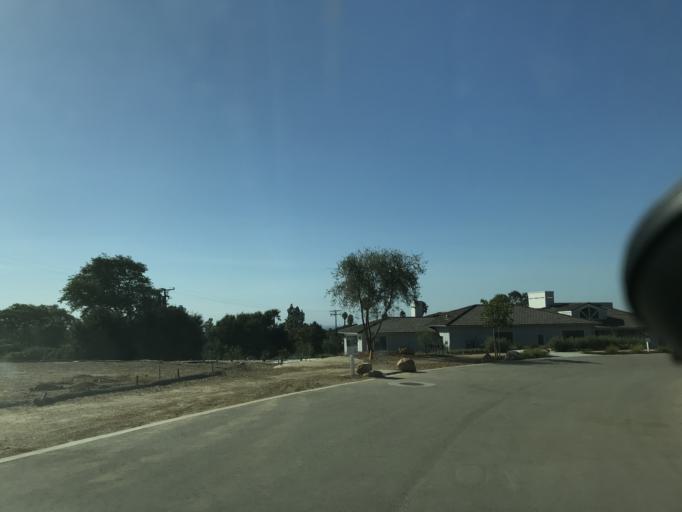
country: US
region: California
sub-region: Santa Barbara County
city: Goleta
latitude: 34.4576
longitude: -119.7853
